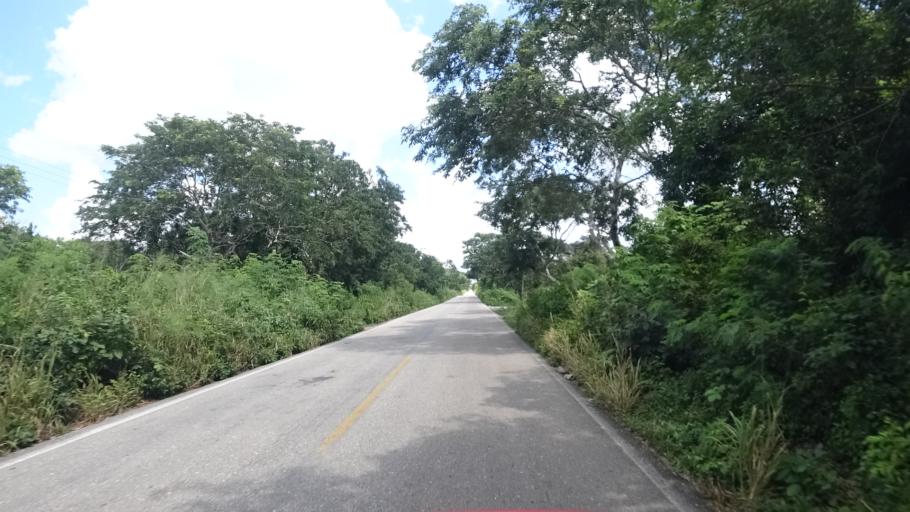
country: MX
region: Yucatan
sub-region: Panaba
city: Loche
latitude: 21.3922
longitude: -88.1421
